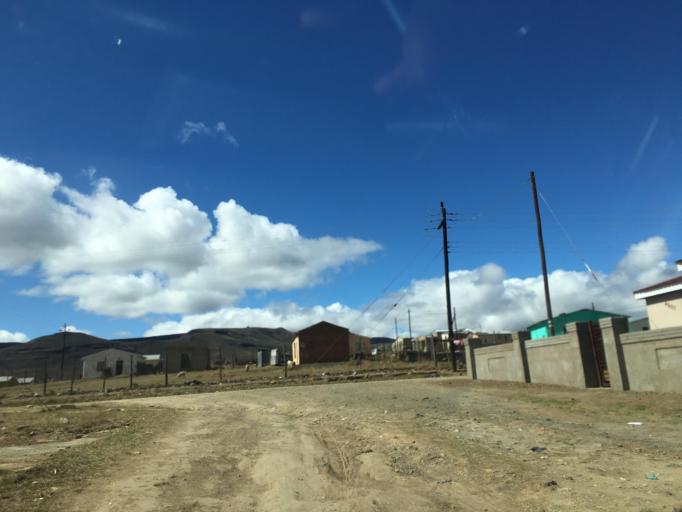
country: ZA
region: Eastern Cape
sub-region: Chris Hani District Municipality
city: Cala
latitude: -31.5394
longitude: 27.6804
